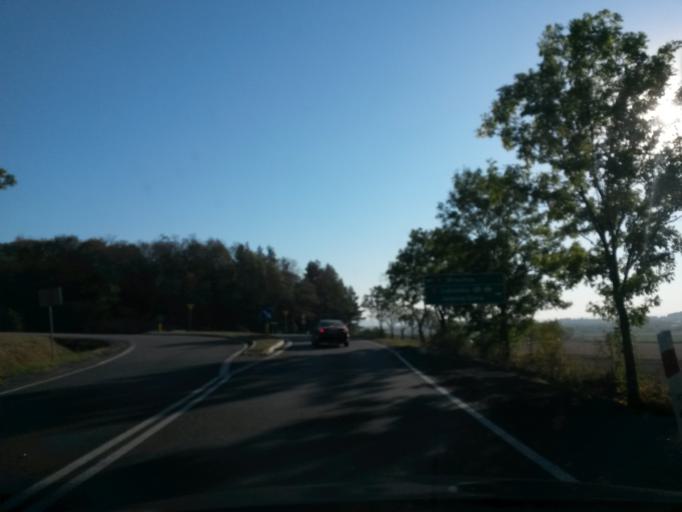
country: PL
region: Lower Silesian Voivodeship
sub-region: Powiat swidnicki
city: Strzegom
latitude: 50.9869
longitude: 16.3826
